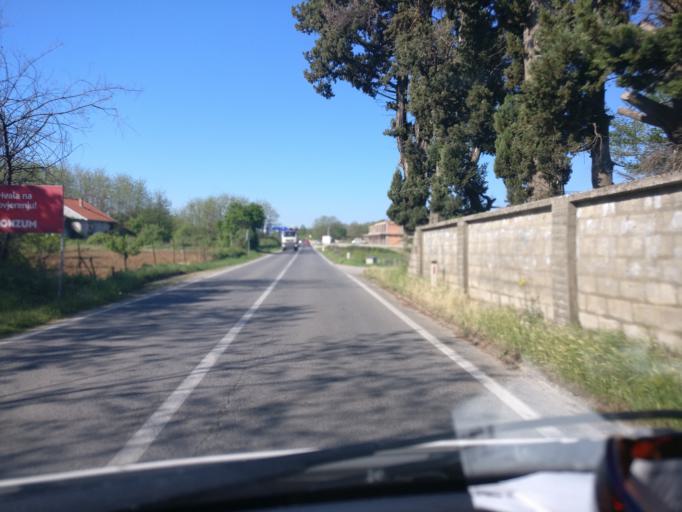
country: BA
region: Federation of Bosnia and Herzegovina
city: Tasovcici
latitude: 43.1356
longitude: 17.7759
